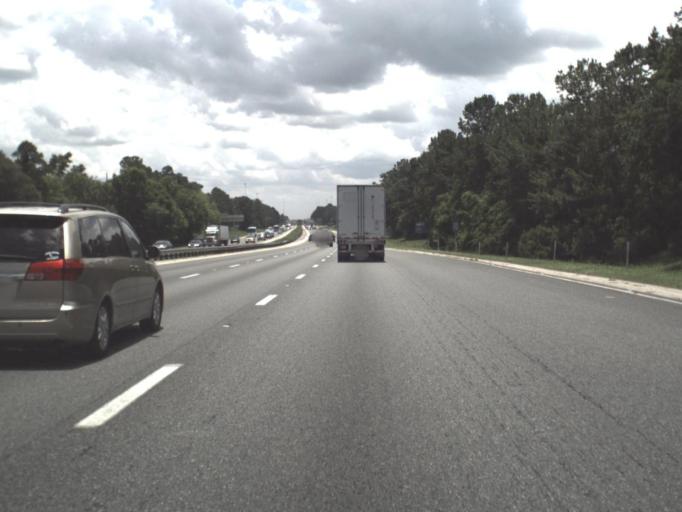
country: US
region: Florida
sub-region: Alachua County
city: Gainesville
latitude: 29.6131
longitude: -82.3832
